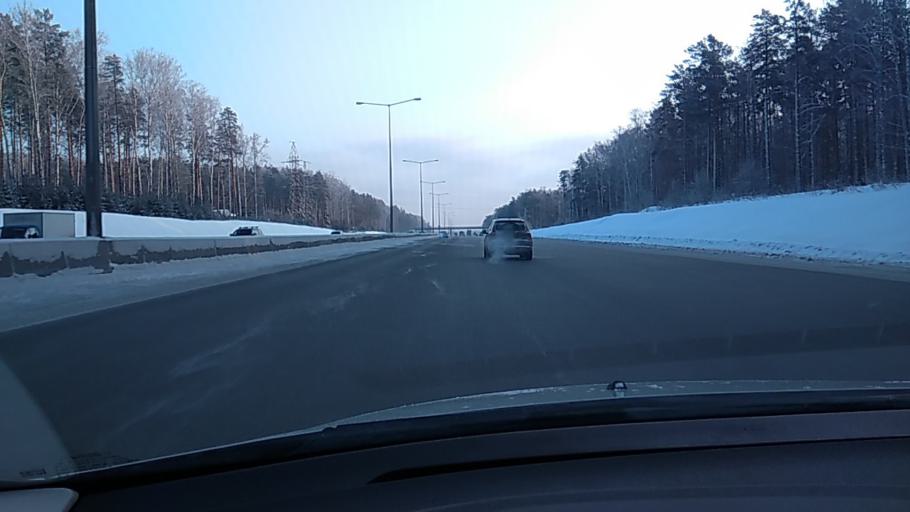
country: RU
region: Sverdlovsk
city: Istok
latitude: 56.7855
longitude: 60.6876
